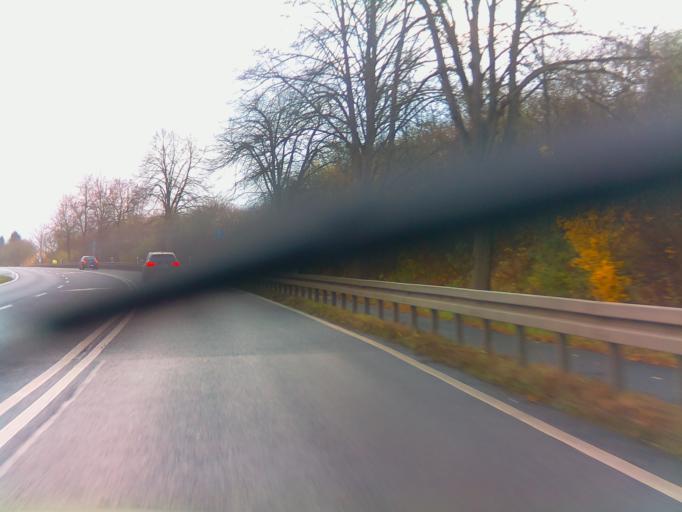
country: DE
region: Hesse
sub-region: Regierungsbezirk Kassel
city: Petersberg
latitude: 50.5523
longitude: 9.6991
